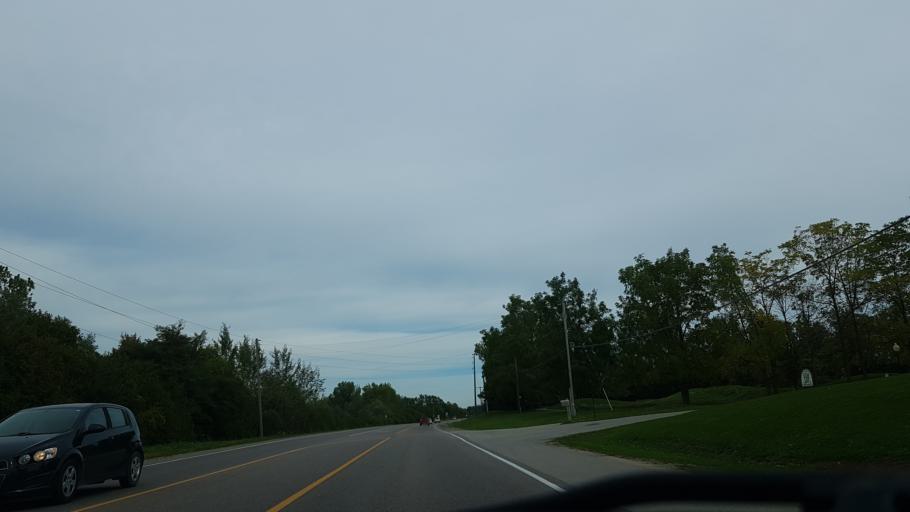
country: CA
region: Ontario
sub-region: Wellington County
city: Guelph
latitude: 43.6015
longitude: -80.2316
